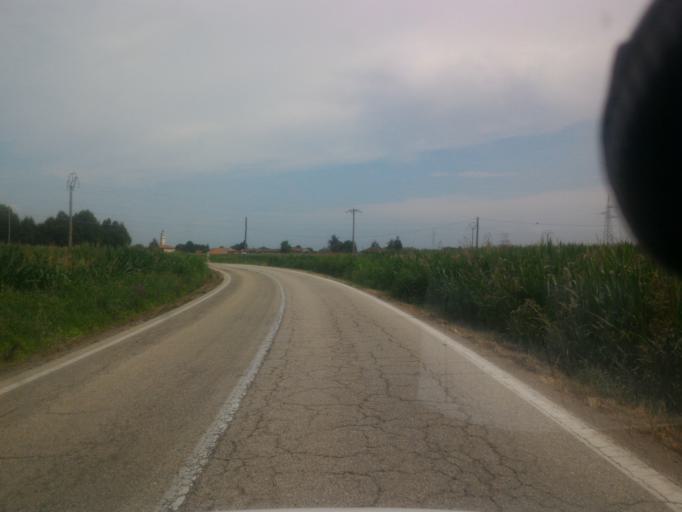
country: IT
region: Piedmont
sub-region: Provincia di Torino
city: Buriasco
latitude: 44.8560
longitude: 7.4418
